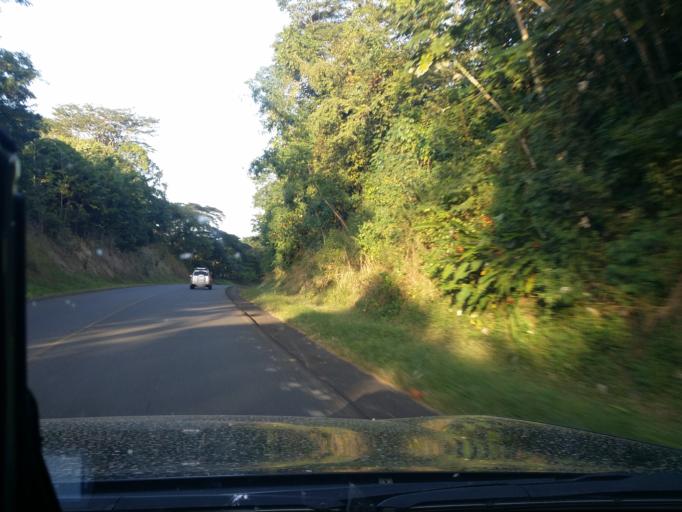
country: NI
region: Rio San Juan
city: San Miguelito
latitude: 11.4911
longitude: -84.8418
